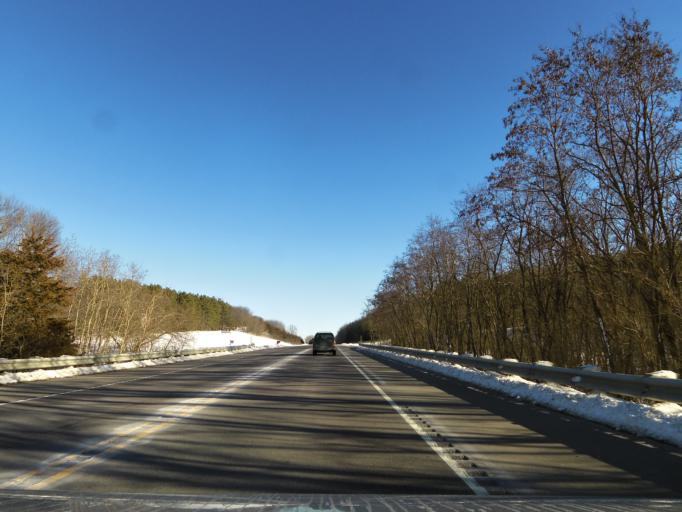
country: US
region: Wisconsin
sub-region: Columbia County
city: Portage
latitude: 43.5093
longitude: -89.5704
